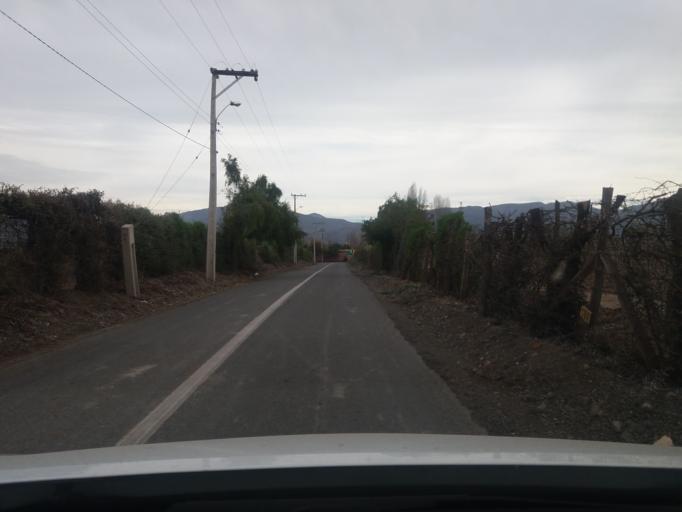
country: CL
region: Valparaiso
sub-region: Provincia de Los Andes
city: Los Andes
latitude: -32.8521
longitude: -70.6389
